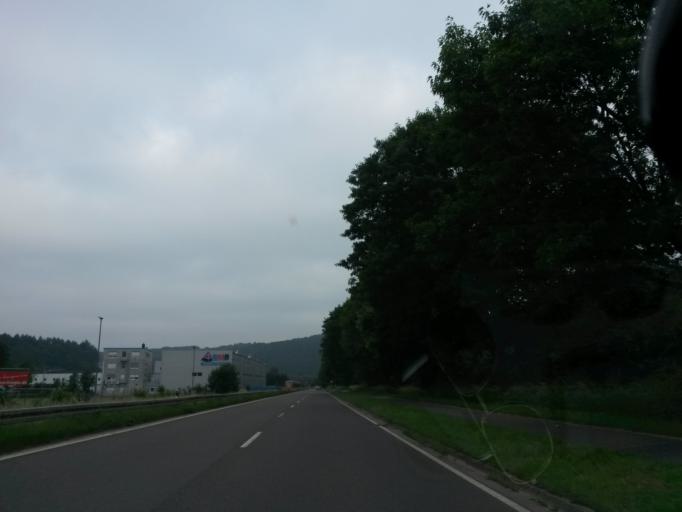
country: DE
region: North Rhine-Westphalia
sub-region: Regierungsbezirk Koln
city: Engelskirchen
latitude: 50.9748
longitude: 7.3589
